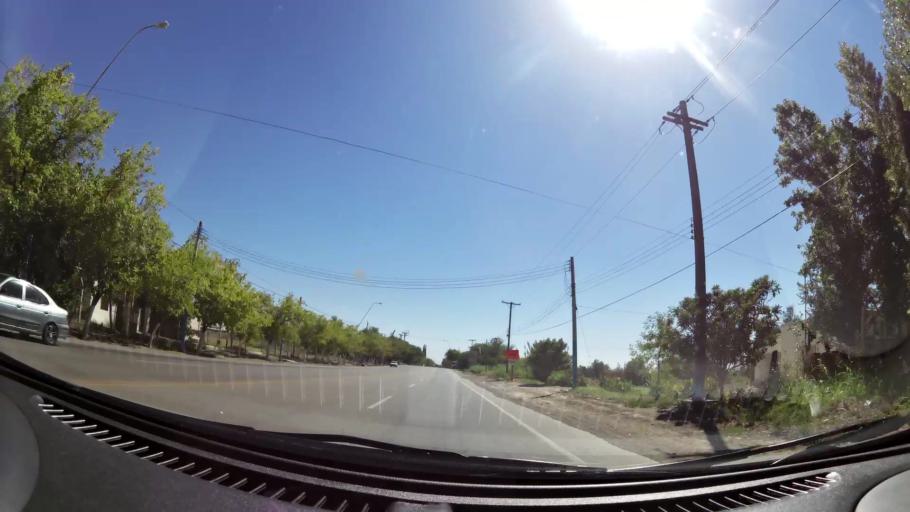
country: AR
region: San Juan
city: Villa Krause
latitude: -31.6029
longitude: -68.5429
